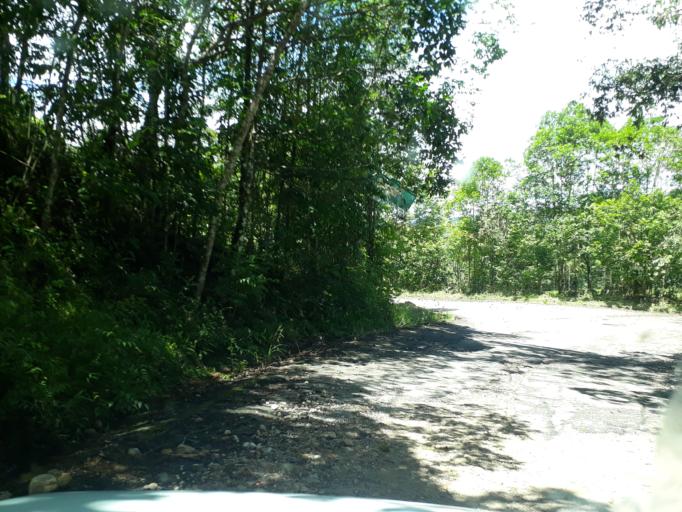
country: CO
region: Cundinamarca
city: Medina
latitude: 4.5764
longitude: -73.3250
